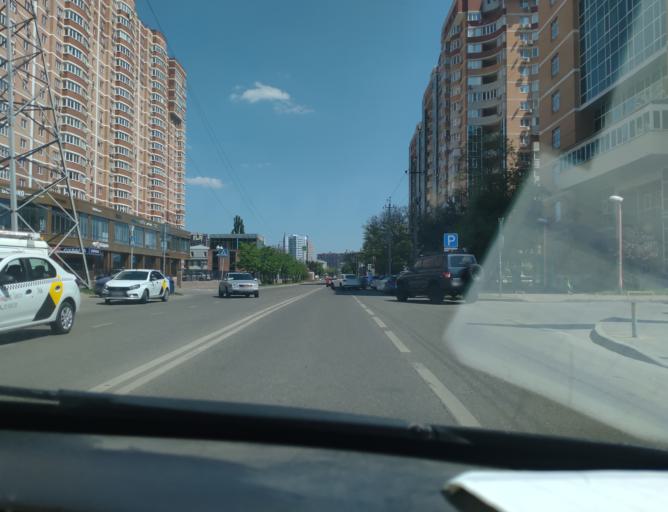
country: RU
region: Krasnodarskiy
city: Krasnodar
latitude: 45.0613
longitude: 38.9637
